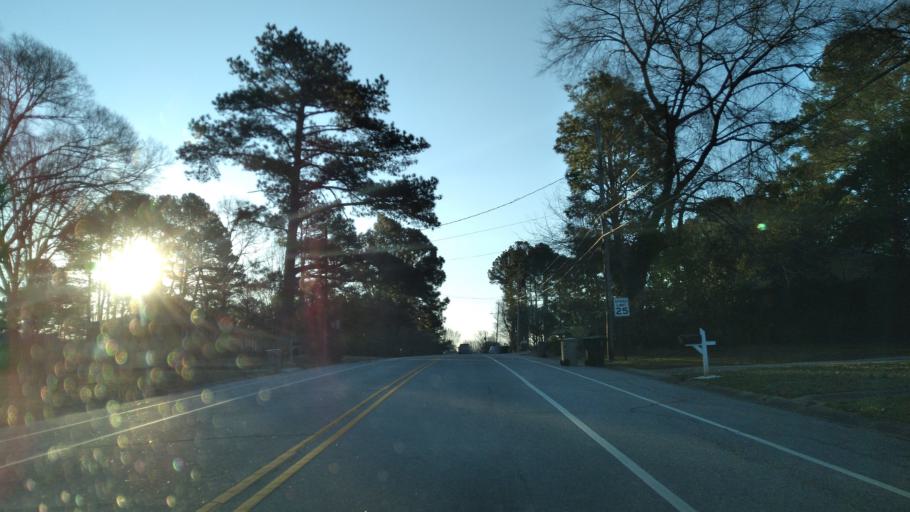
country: US
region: North Carolina
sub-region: Wake County
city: Garner
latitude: 35.6994
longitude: -78.6225
